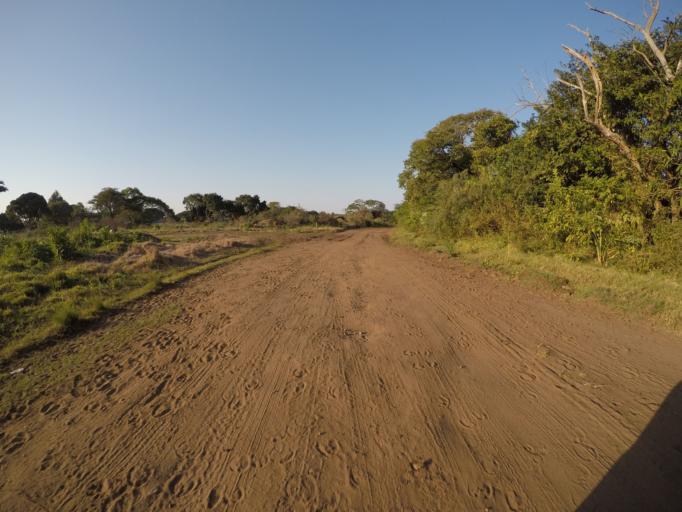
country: ZA
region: KwaZulu-Natal
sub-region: uThungulu District Municipality
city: KwaMbonambi
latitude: -28.6917
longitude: 32.2017
